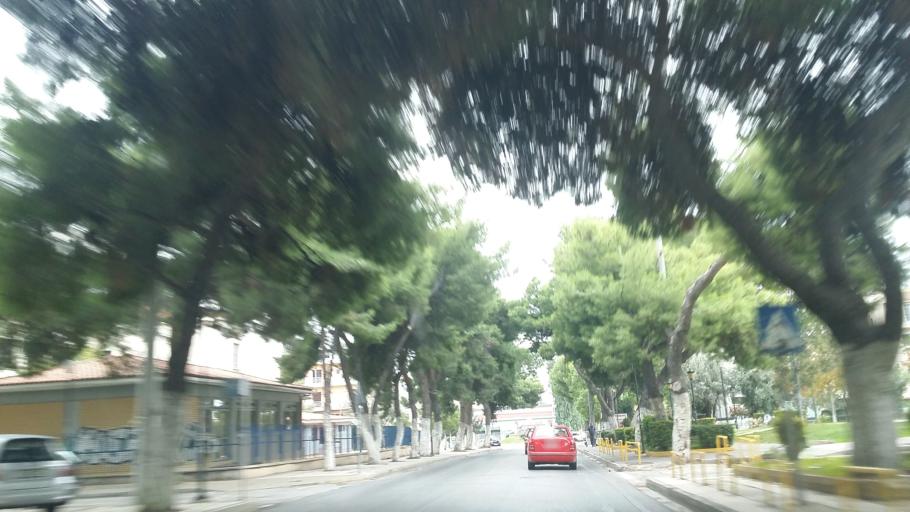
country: GR
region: Attica
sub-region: Nomarchia Athinas
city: Metamorfosi
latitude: 38.0632
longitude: 23.7578
